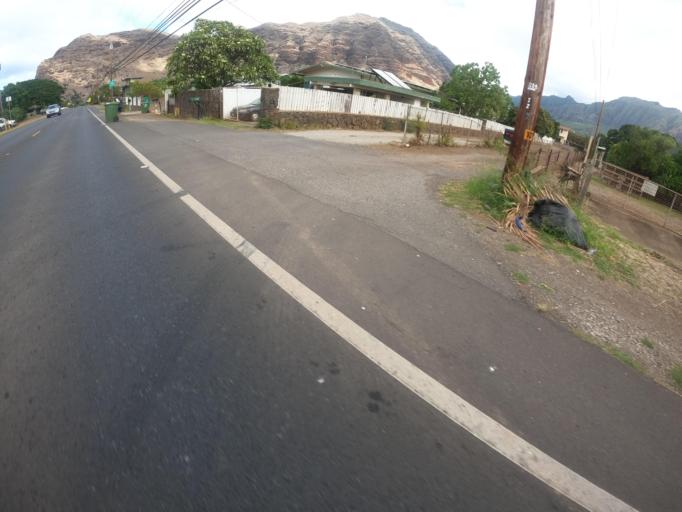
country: US
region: Hawaii
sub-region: Honolulu County
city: Makaha
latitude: 21.4699
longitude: -158.2159
